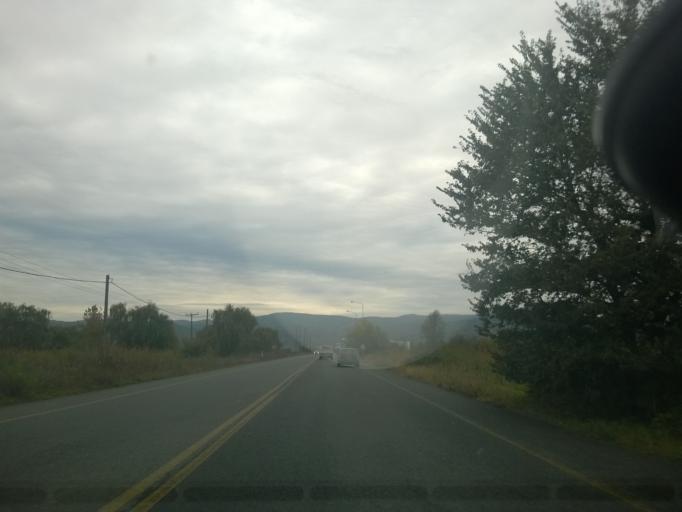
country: GR
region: Central Macedonia
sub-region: Nomos Pellis
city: Apsalos
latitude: 40.9122
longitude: 22.0726
